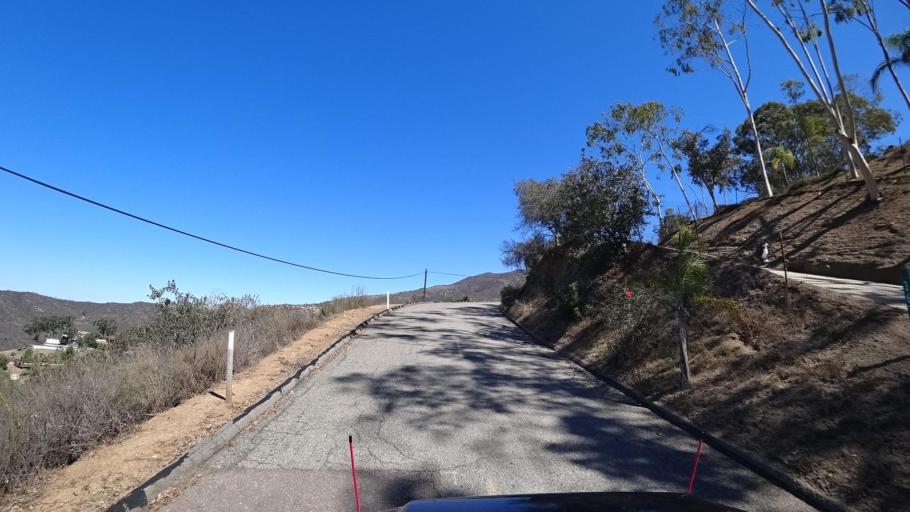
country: US
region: California
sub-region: San Diego County
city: Jamul
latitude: 32.7395
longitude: -116.8777
